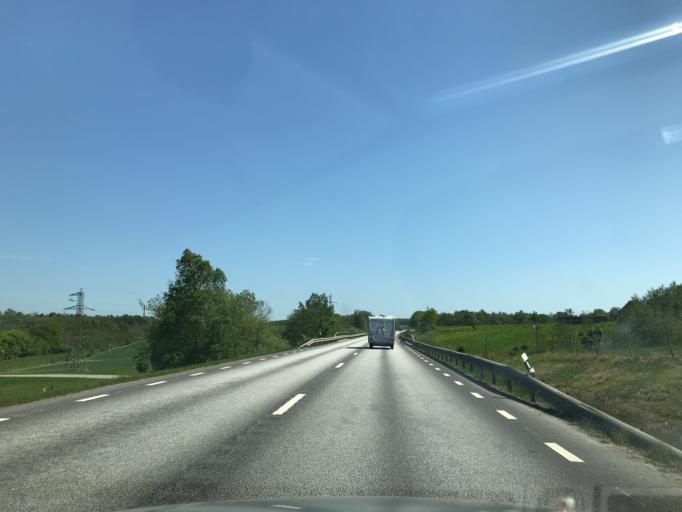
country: SE
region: Skane
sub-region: Klippans Kommun
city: Klippan
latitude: 56.1184
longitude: 13.1257
